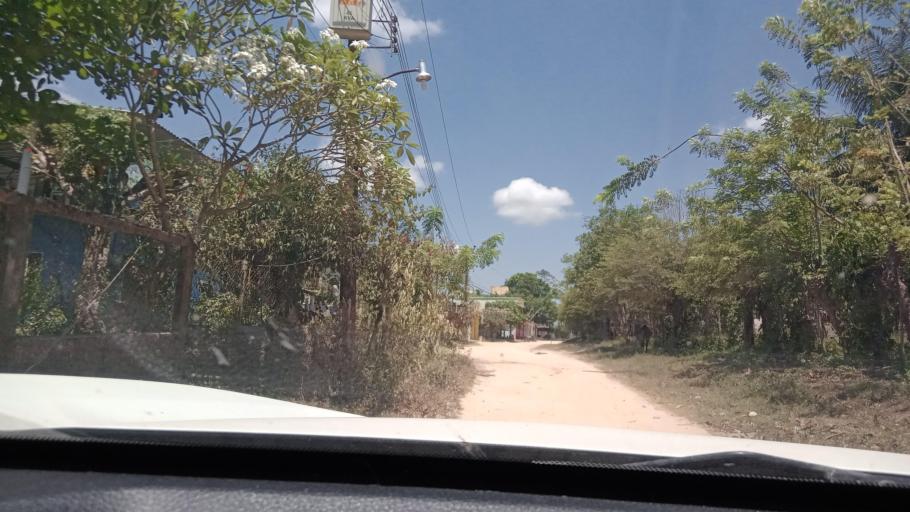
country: MX
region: Veracruz
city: Las Choapas
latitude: 17.7542
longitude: -94.1112
